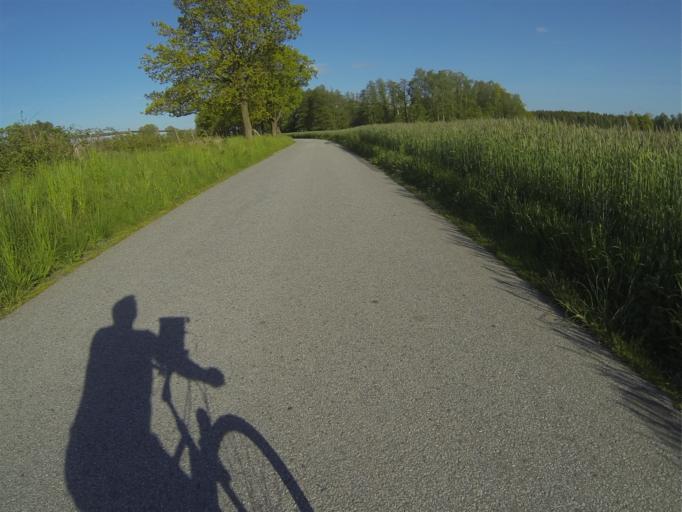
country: SE
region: Skane
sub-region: Hoors Kommun
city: Loberod
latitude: 55.7259
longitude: 13.3941
